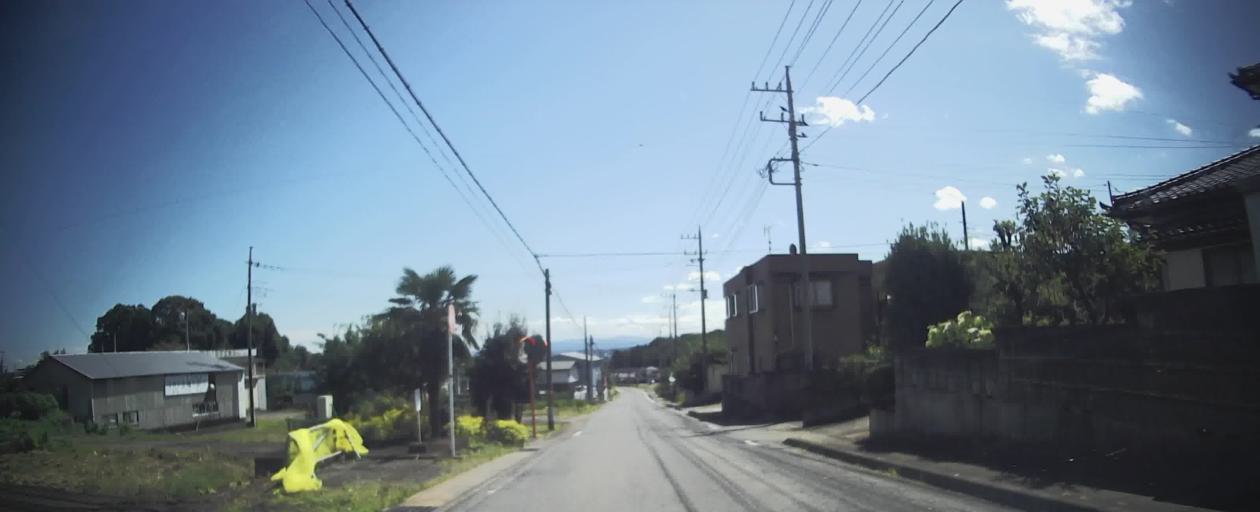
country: JP
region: Gunma
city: Kanekomachi
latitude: 36.4078
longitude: 138.9528
